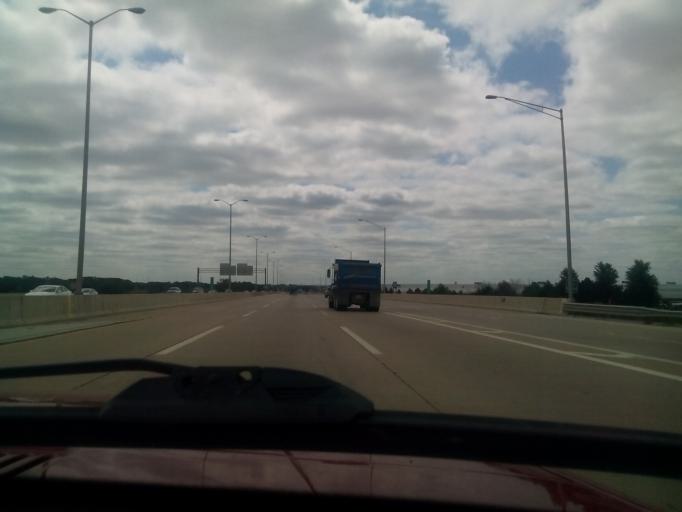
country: US
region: Illinois
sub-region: Cook County
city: Lemont
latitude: 41.6958
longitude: -88.0302
